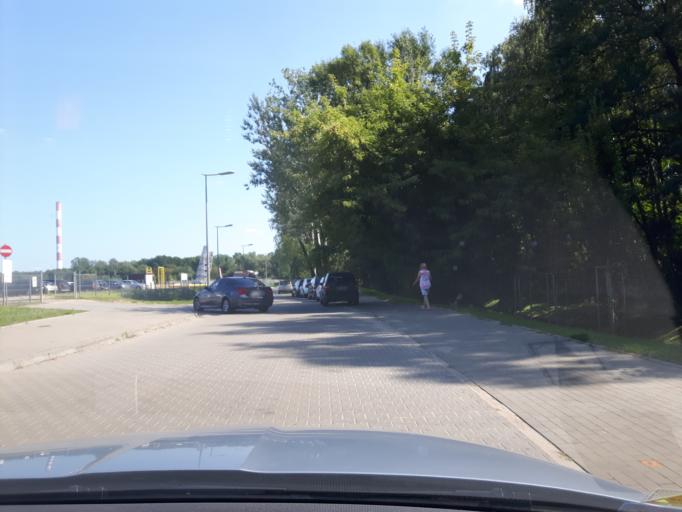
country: PL
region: Masovian Voivodeship
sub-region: Powiat wolominski
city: Zabki
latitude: 52.2693
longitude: 21.0962
